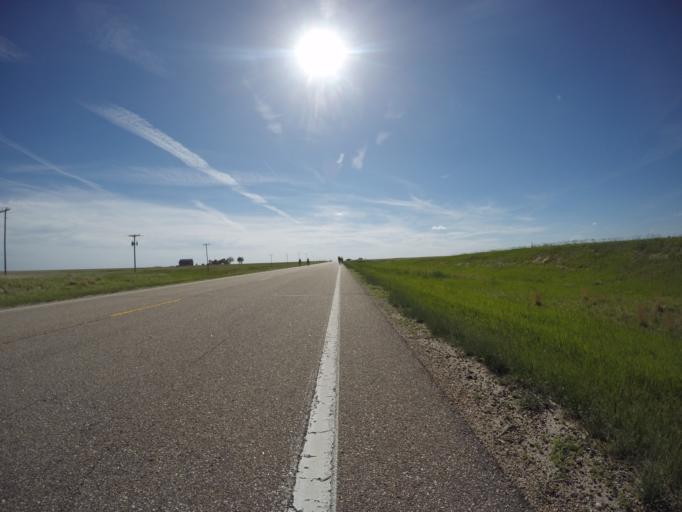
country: US
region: Kansas
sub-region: Cheyenne County
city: Saint Francis
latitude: 39.7566
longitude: -101.9816
